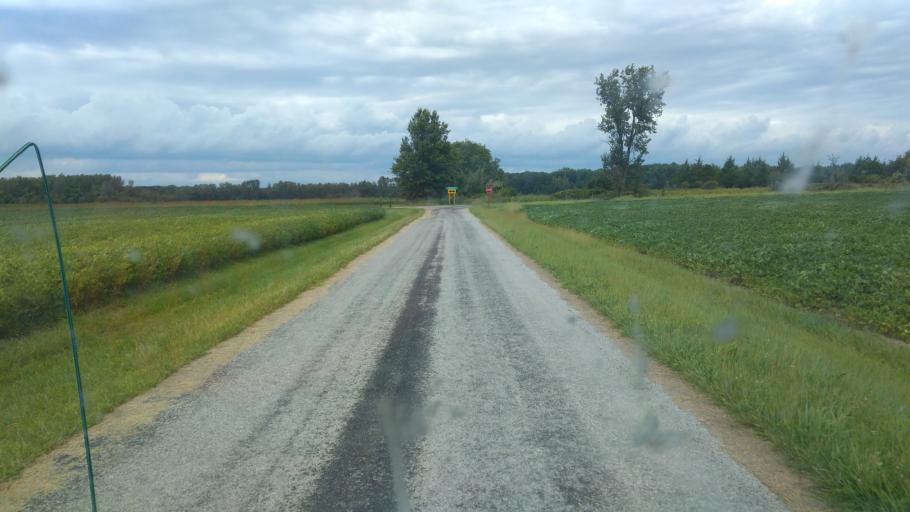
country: US
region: Ohio
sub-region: Wyandot County
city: Upper Sandusky
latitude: 40.7013
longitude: -83.2656
